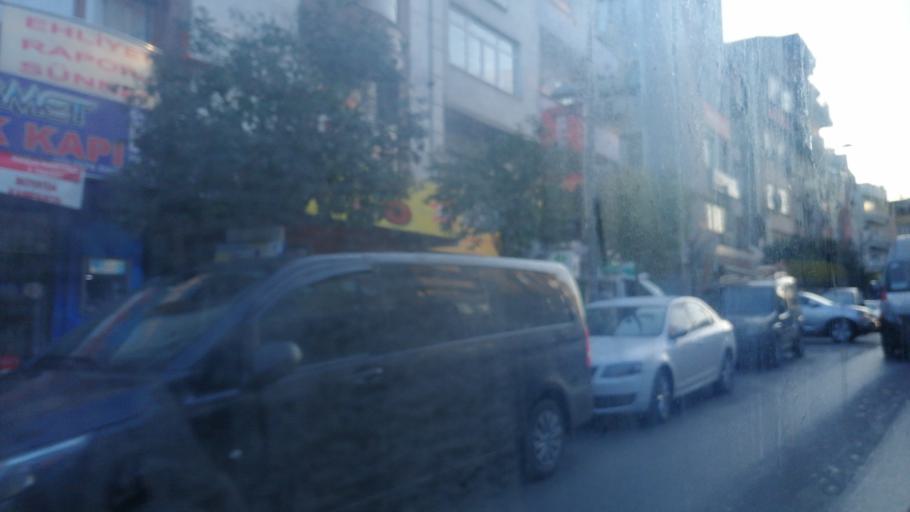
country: TR
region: Istanbul
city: Sisli
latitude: 41.0818
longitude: 28.9916
